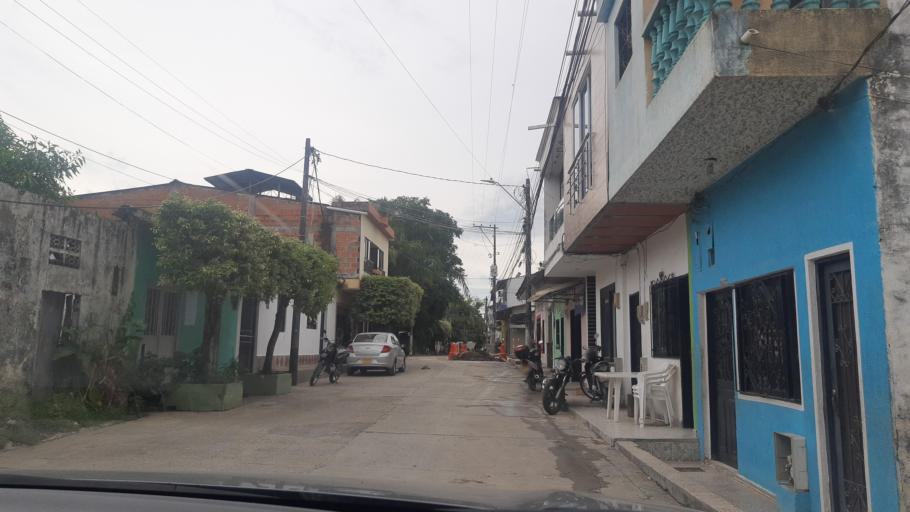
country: CO
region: Antioquia
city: Puerto Triunfo
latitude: 5.8719
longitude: -74.6400
